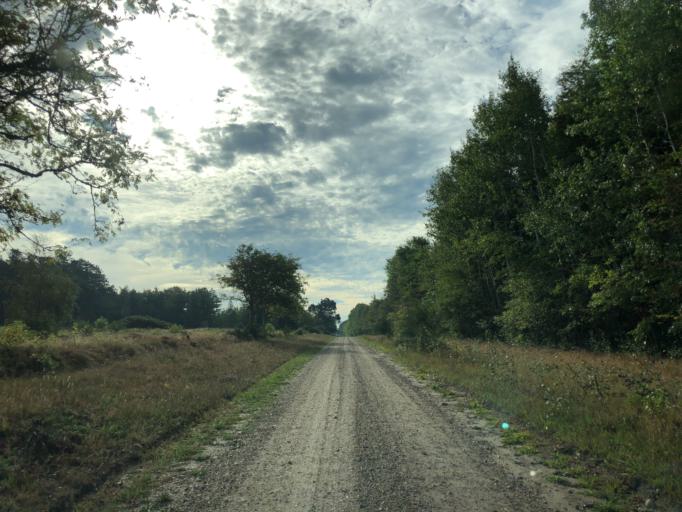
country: DK
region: Central Jutland
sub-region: Holstebro Kommune
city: Ulfborg
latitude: 56.1762
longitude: 8.3640
